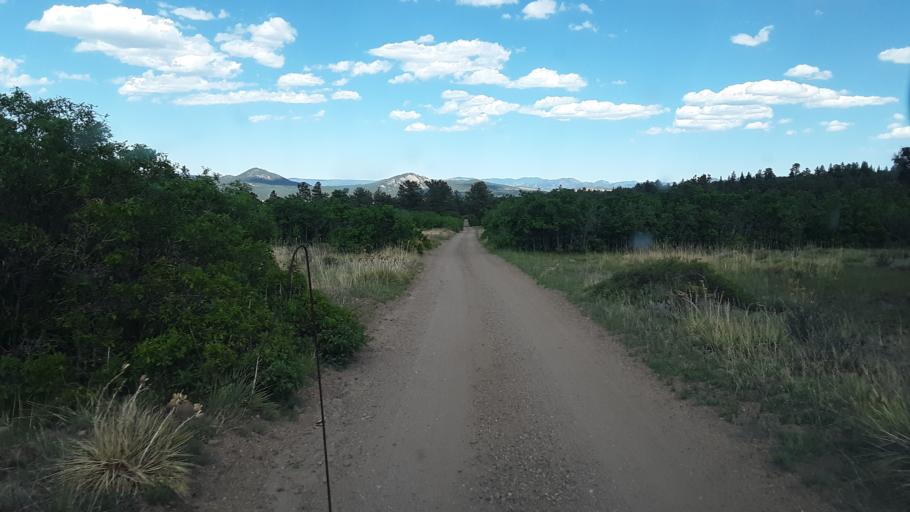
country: US
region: Colorado
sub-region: Custer County
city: Westcliffe
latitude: 38.2218
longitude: -105.6110
